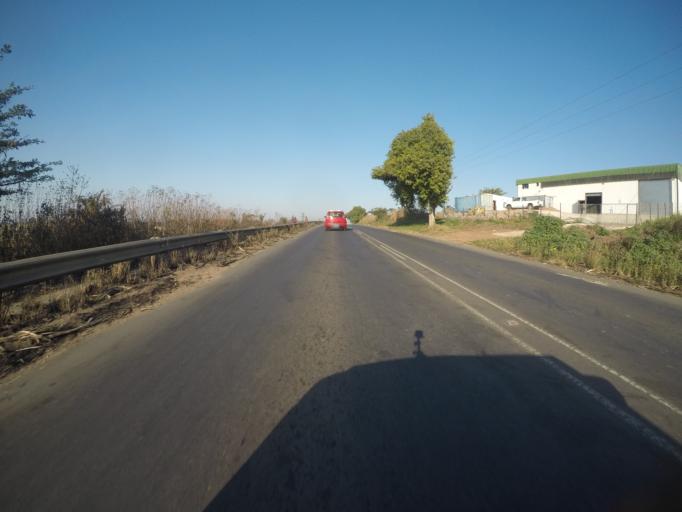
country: ZA
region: KwaZulu-Natal
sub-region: iLembe District Municipality
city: Stanger
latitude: -29.4085
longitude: 31.2471
